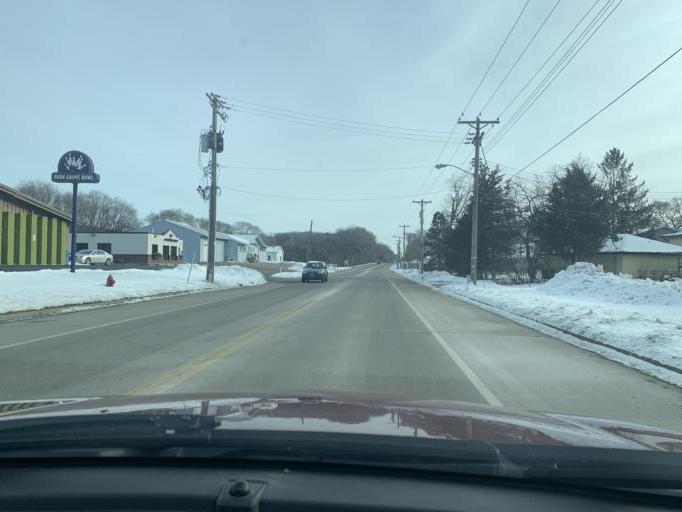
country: US
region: Minnesota
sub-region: Washington County
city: Saint Paul Park
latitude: 44.8392
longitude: -92.9766
